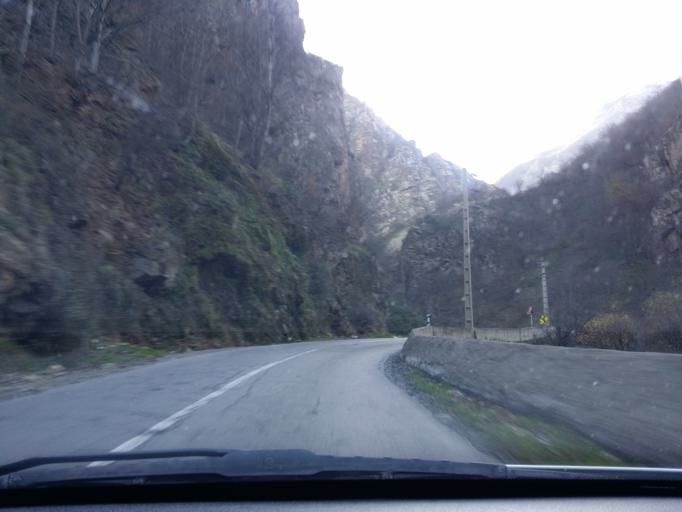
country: IR
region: Mazandaran
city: Chalus
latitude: 36.2886
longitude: 51.2419
